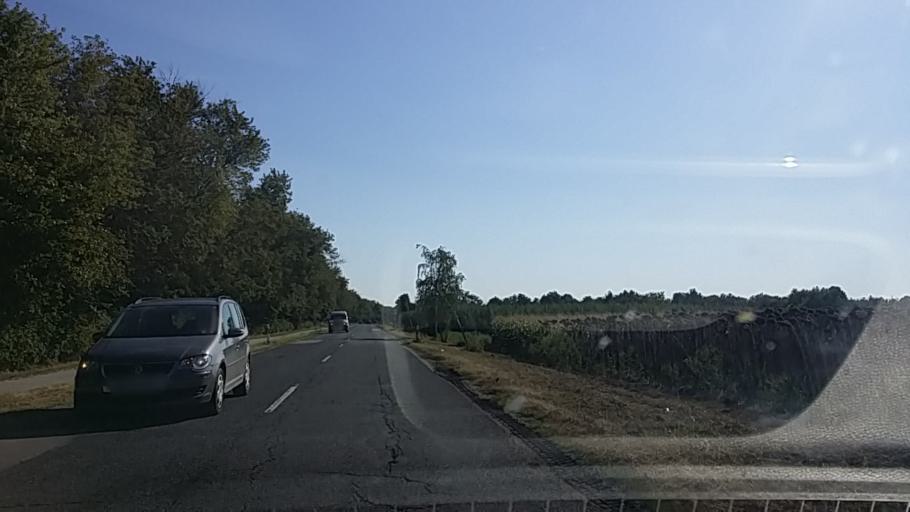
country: AT
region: Burgenland
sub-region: Politischer Bezirk Neusiedl am See
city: Pamhagen
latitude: 47.6653
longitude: 16.9013
